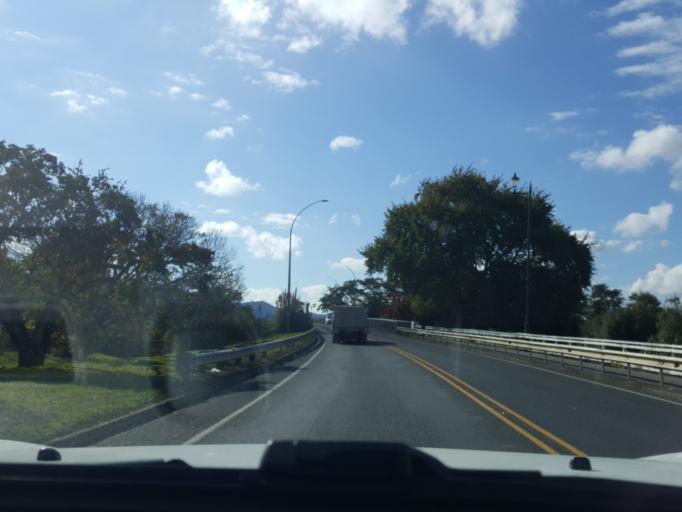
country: NZ
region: Waikato
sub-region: Waikato District
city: Ngaruawahia
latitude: -37.6638
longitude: 175.1486
